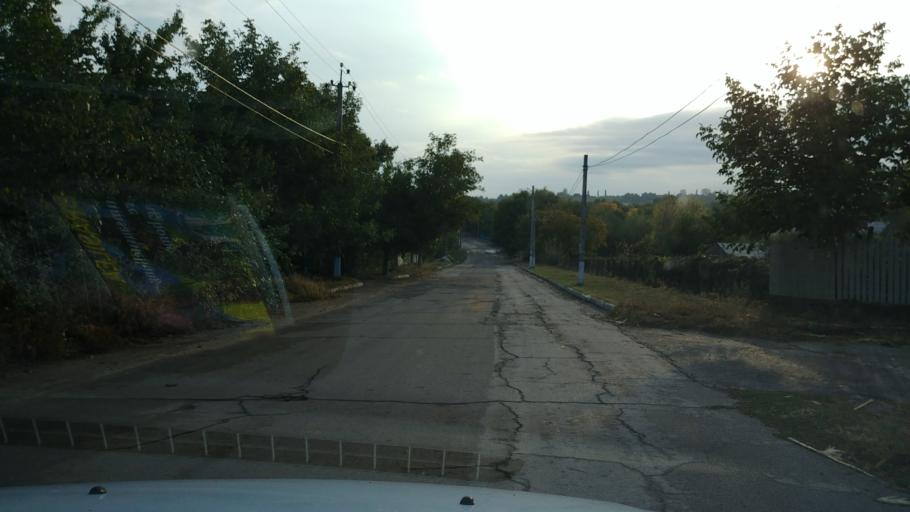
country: MD
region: Rezina
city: Saharna
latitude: 47.6768
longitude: 28.9621
